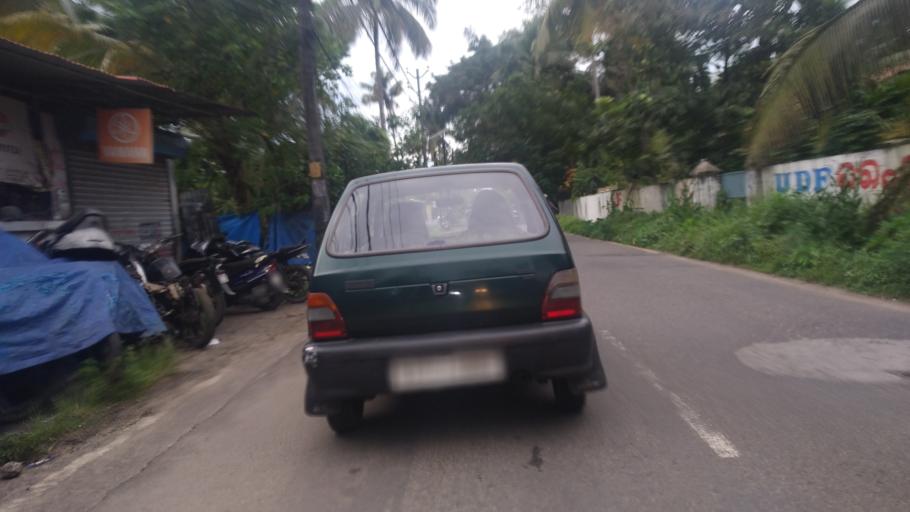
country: IN
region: Kerala
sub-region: Ernakulam
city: Cochin
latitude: 9.8829
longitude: 76.2621
